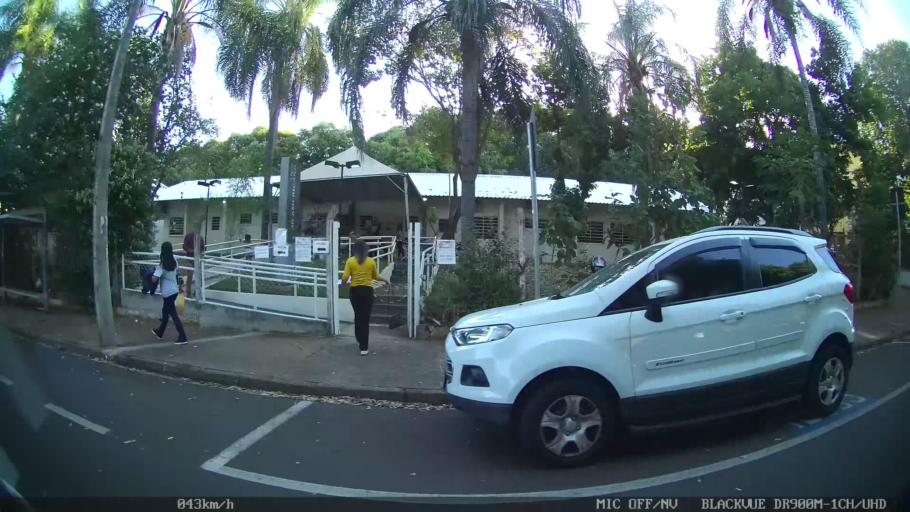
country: BR
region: Sao Paulo
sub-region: Sao Jose Do Rio Preto
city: Sao Jose do Rio Preto
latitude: -20.7999
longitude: -49.3595
